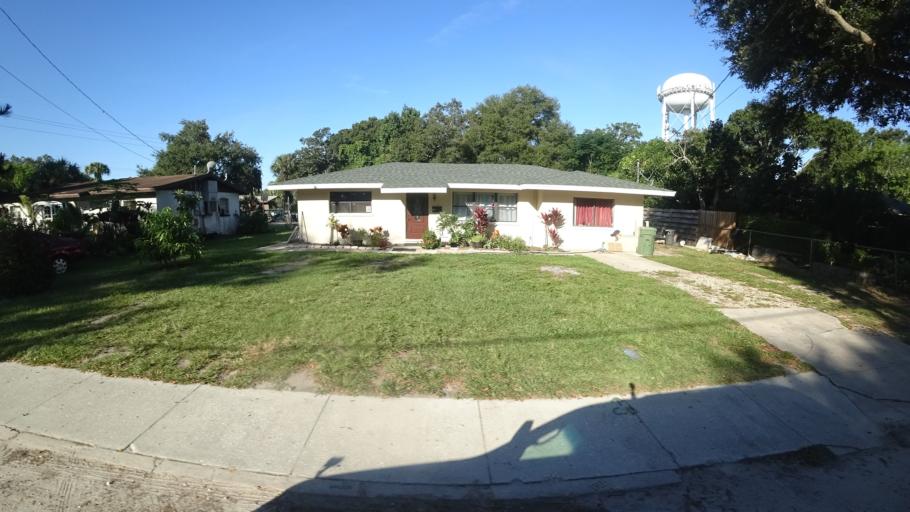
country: US
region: Florida
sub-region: Manatee County
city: Samoset
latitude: 27.4921
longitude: -82.5396
